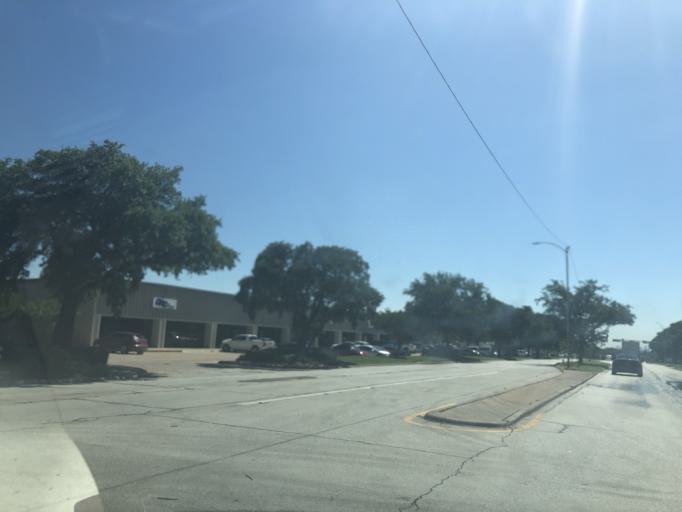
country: US
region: Texas
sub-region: Dallas County
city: Grand Prairie
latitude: 32.7853
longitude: -97.0440
